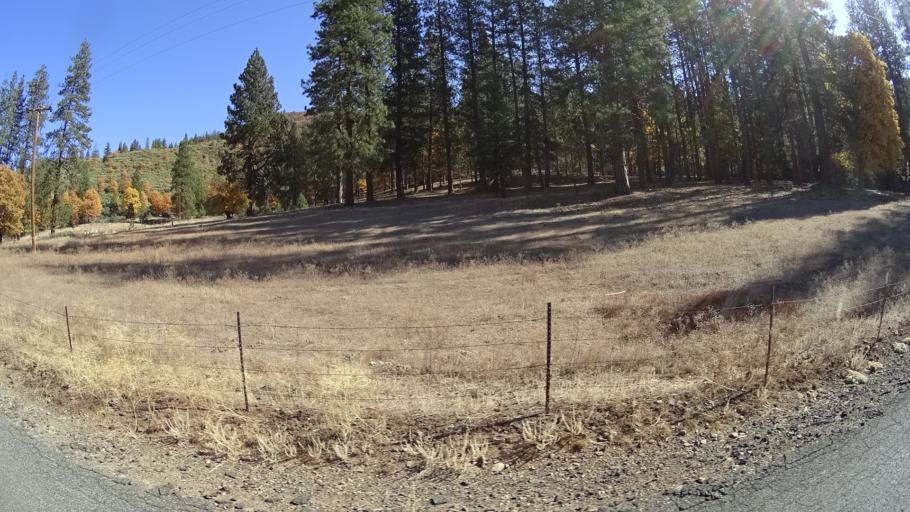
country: US
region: California
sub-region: Siskiyou County
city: Yreka
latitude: 41.5861
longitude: -122.9565
